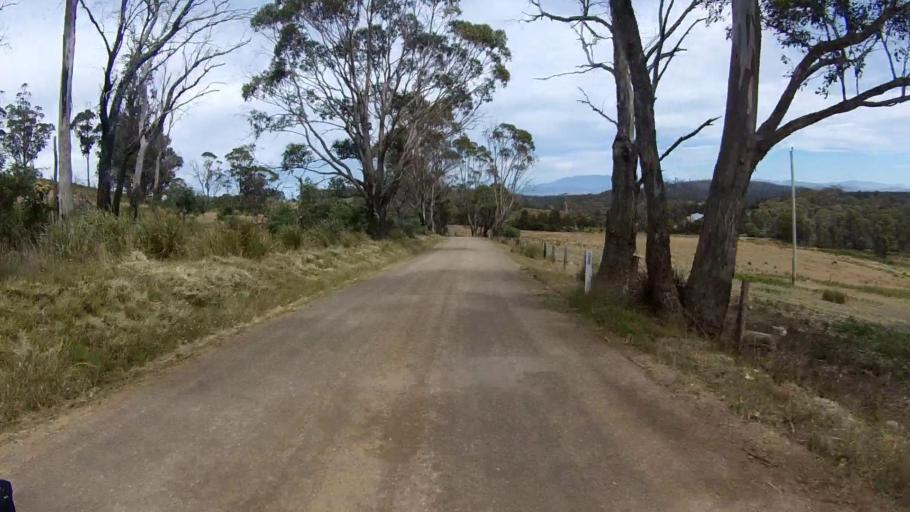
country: AU
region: Tasmania
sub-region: Sorell
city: Sorell
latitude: -42.7895
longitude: 147.7002
